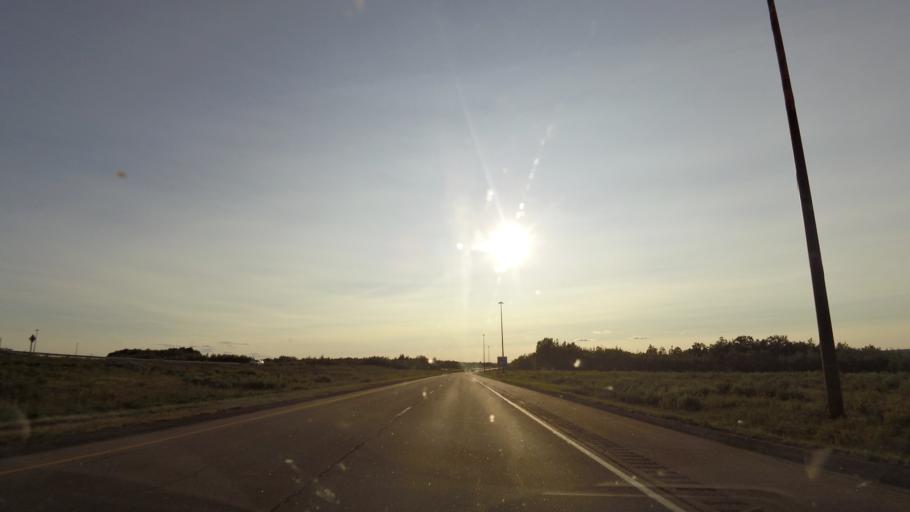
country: CA
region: New Brunswick
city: Dieppe
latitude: 46.1278
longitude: -64.6828
